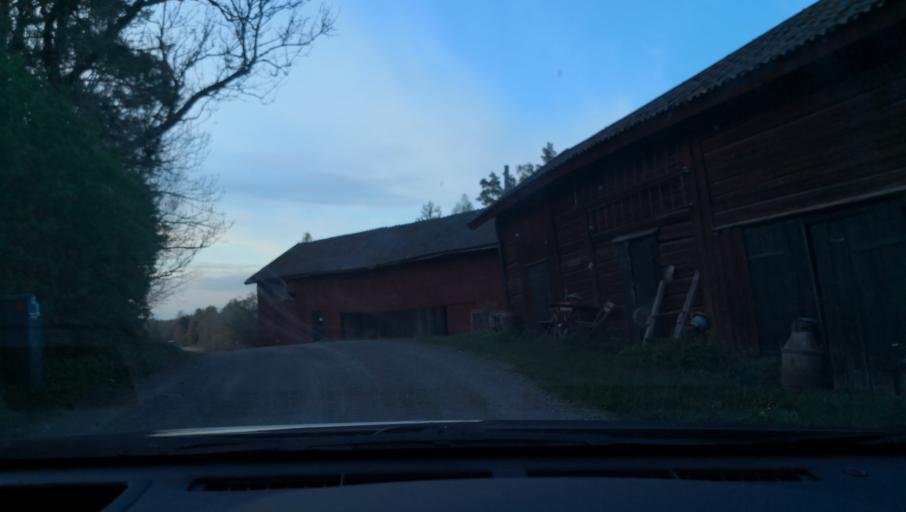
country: SE
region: OErebro
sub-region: Askersunds Kommun
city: Askersund
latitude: 58.9673
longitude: 14.9505
